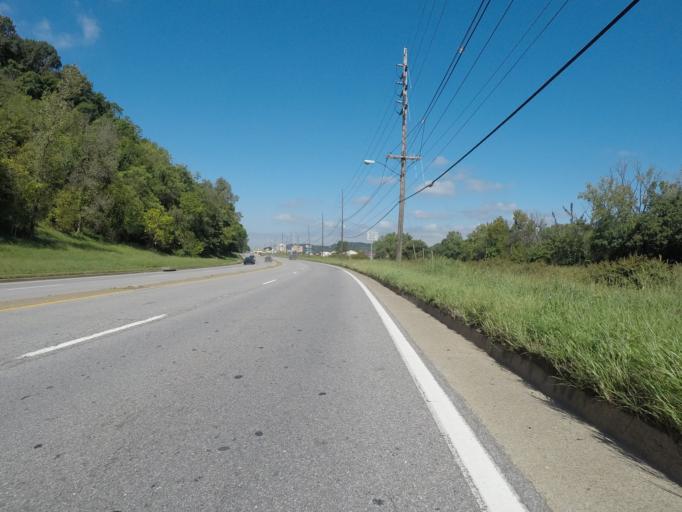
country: US
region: Kentucky
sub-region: Boyd County
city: Ashland
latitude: 38.4612
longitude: -82.6138
